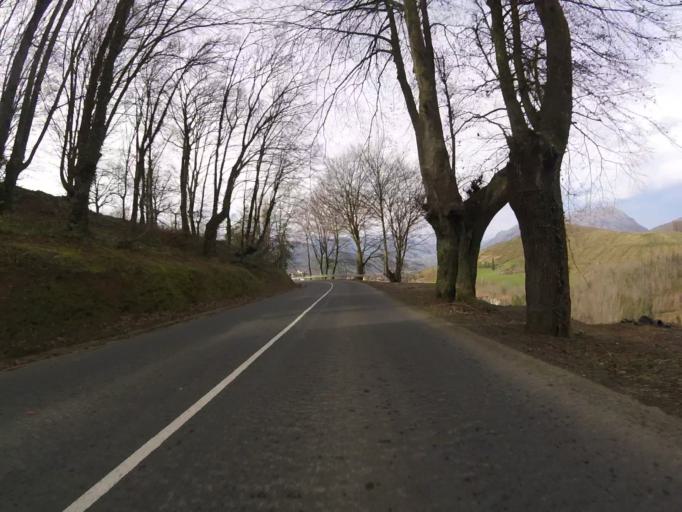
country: ES
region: Basque Country
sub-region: Provincia de Guipuzcoa
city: Beizama
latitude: 43.1683
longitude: -2.2245
